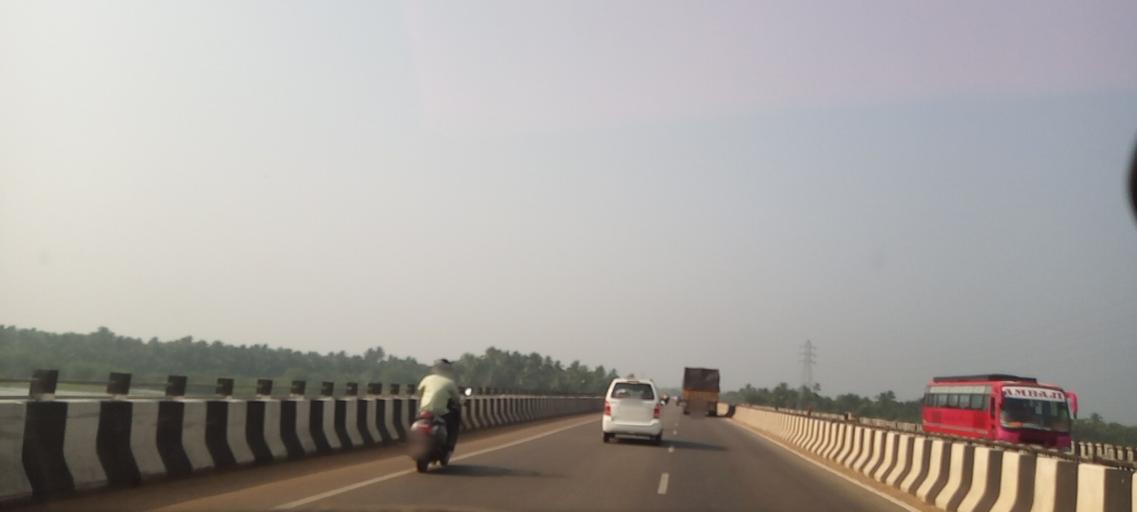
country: IN
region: Karnataka
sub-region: Udupi
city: Coondapoor
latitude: 13.6487
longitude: 74.7049
